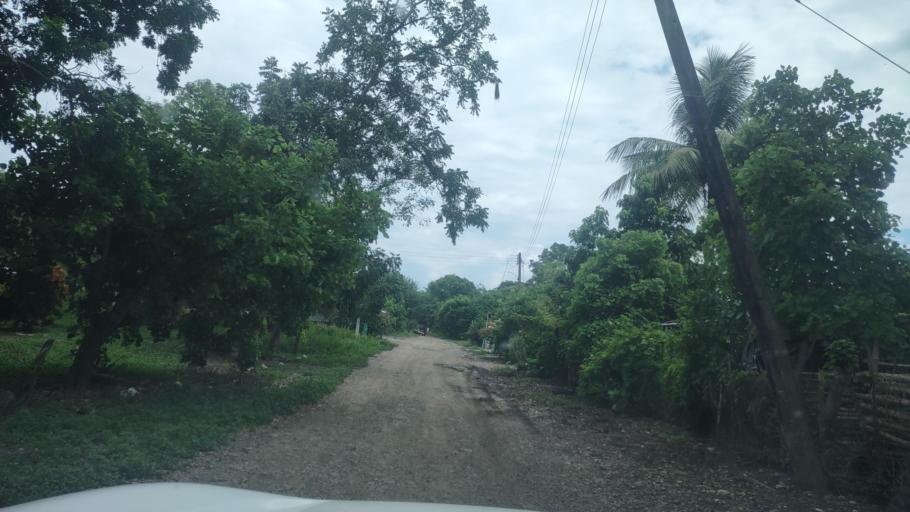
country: MX
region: Veracruz
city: Tepetzintla
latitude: 21.0465
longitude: -97.9988
